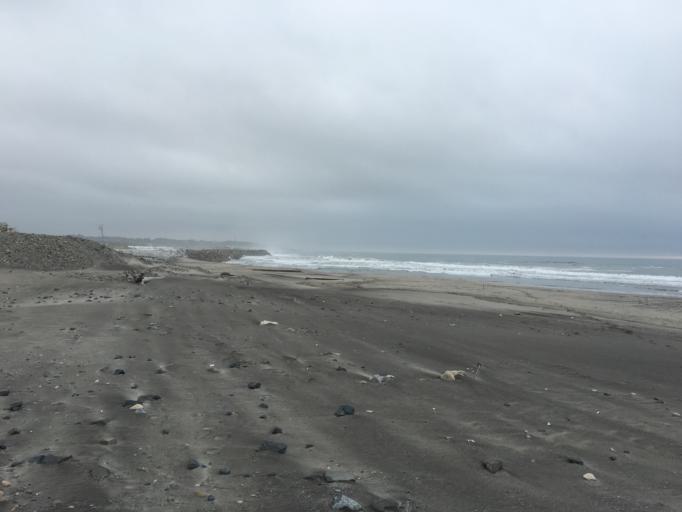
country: JP
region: Fukushima
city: Namie
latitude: 37.6870
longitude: 141.0116
